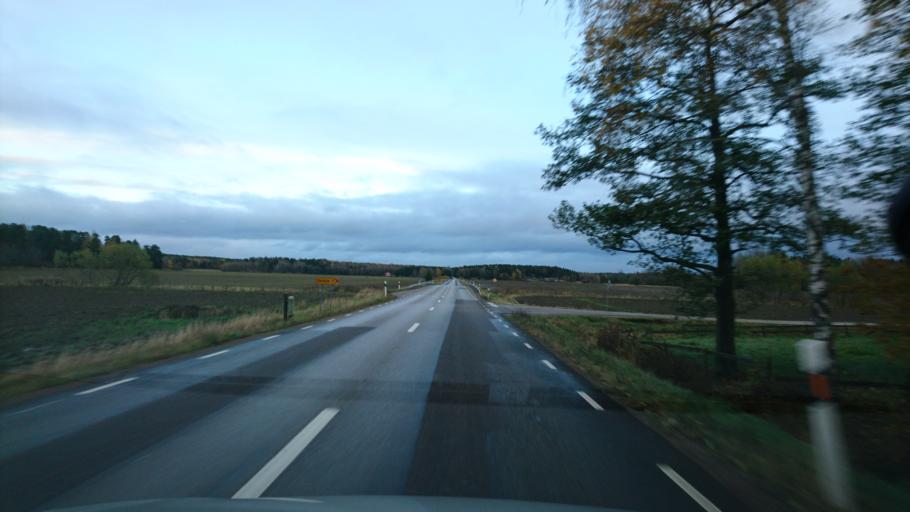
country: SE
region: Uppsala
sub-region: Uppsala Kommun
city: Vattholma
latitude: 59.9504
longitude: 17.9129
